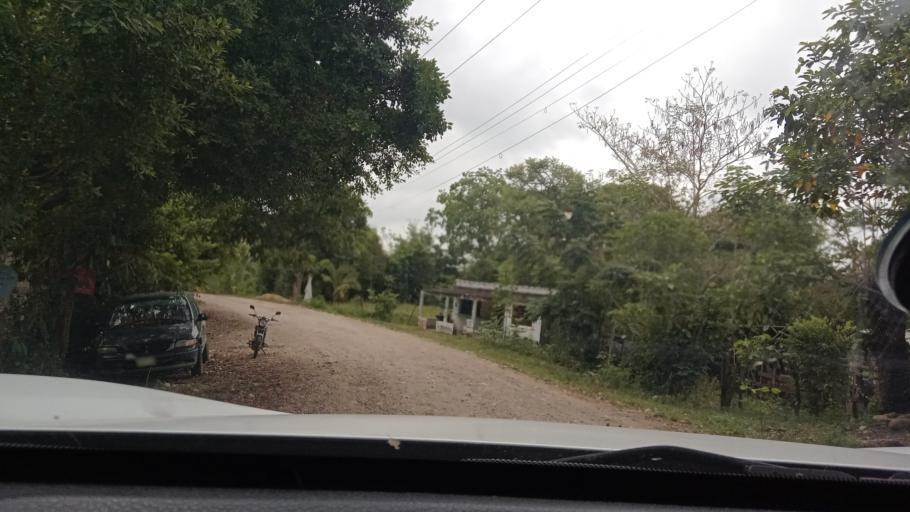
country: MX
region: Tabasco
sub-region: Huimanguillo
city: Francisco Rueda
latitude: 17.5635
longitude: -94.0217
